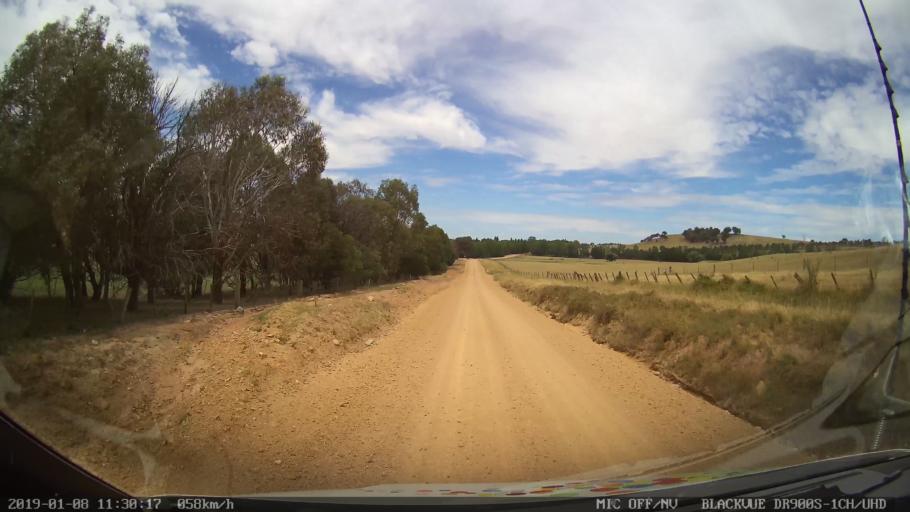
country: AU
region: New South Wales
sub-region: Guyra
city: Guyra
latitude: -30.3066
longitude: 151.5452
